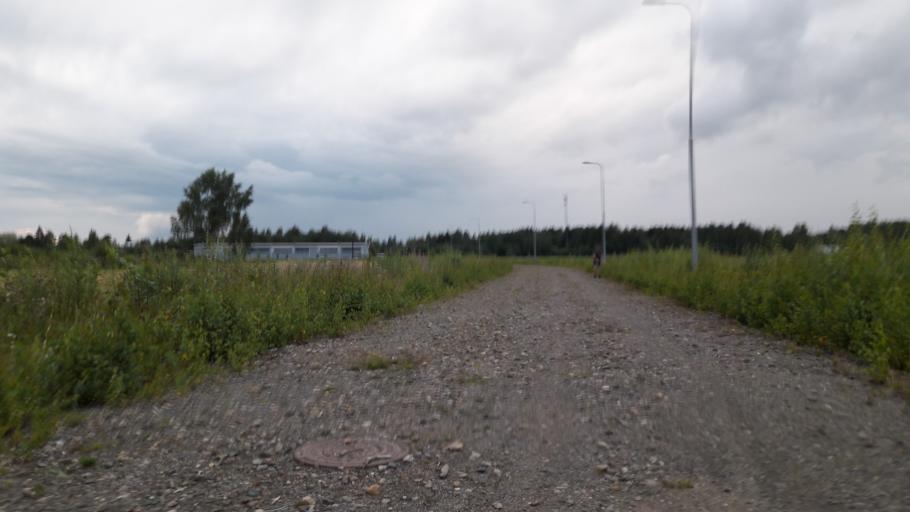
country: FI
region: North Karelia
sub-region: Joensuu
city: Joensuu
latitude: 62.5482
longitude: 29.8397
